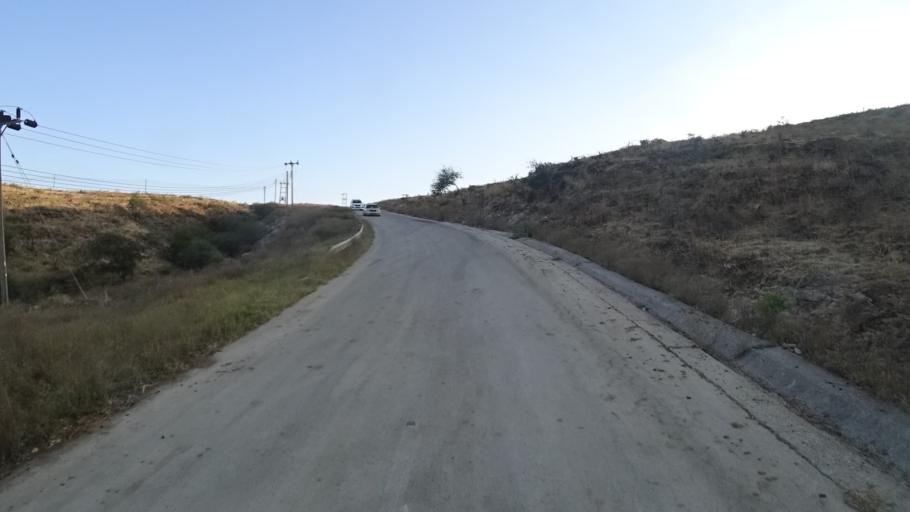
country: OM
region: Zufar
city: Salalah
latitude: 17.1503
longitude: 54.6176
